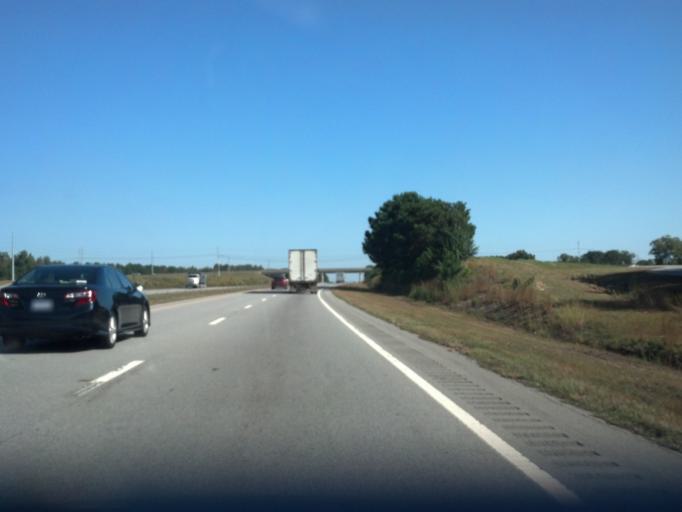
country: US
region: North Carolina
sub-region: Pitt County
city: Summerfield
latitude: 35.6260
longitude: -77.4352
